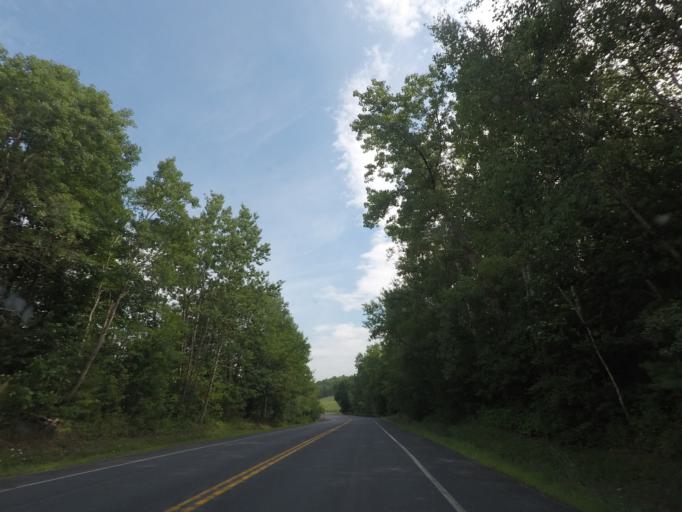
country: US
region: New York
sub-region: Rensselaer County
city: Poestenkill
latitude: 42.6794
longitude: -73.5688
